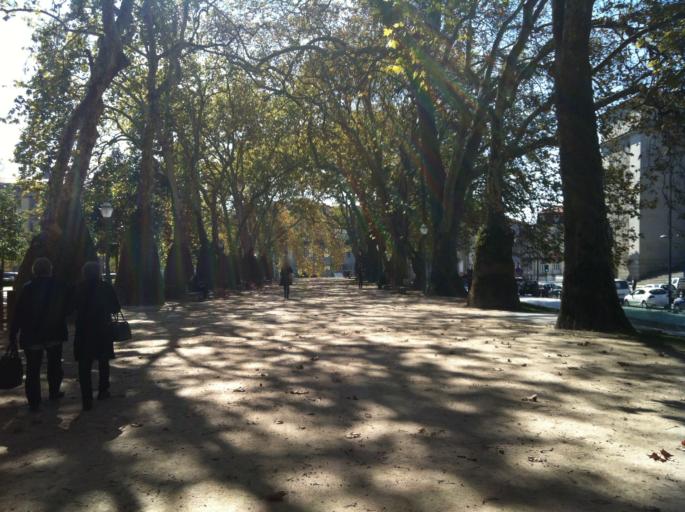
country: PT
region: Porto
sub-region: Porto
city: Porto
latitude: 41.1459
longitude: -8.6172
